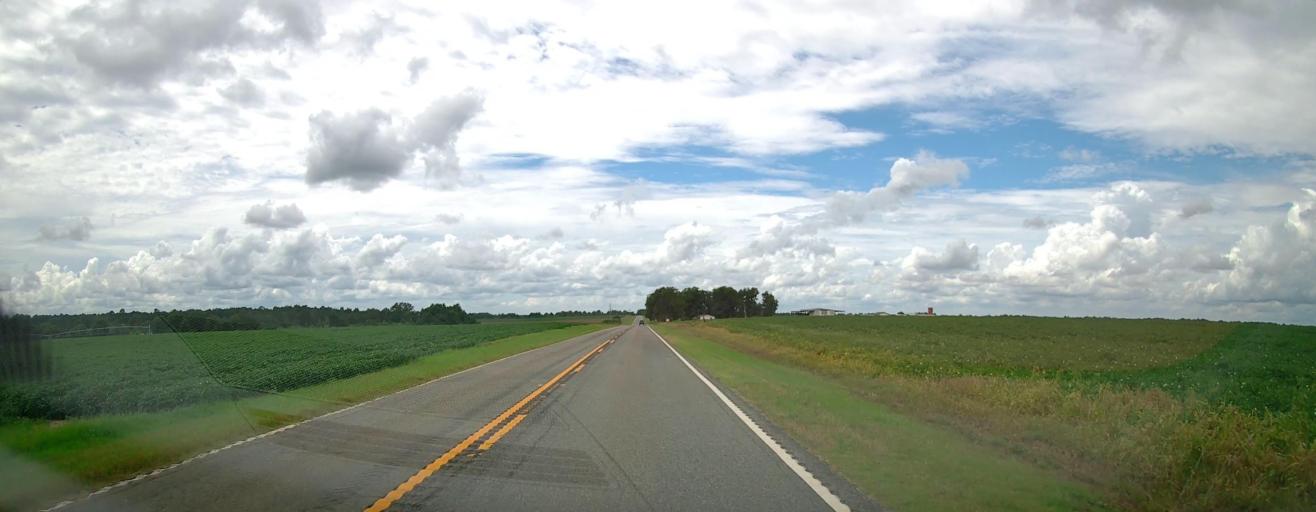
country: US
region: Georgia
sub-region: Dooly County
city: Unadilla
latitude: 32.2588
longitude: -83.7831
